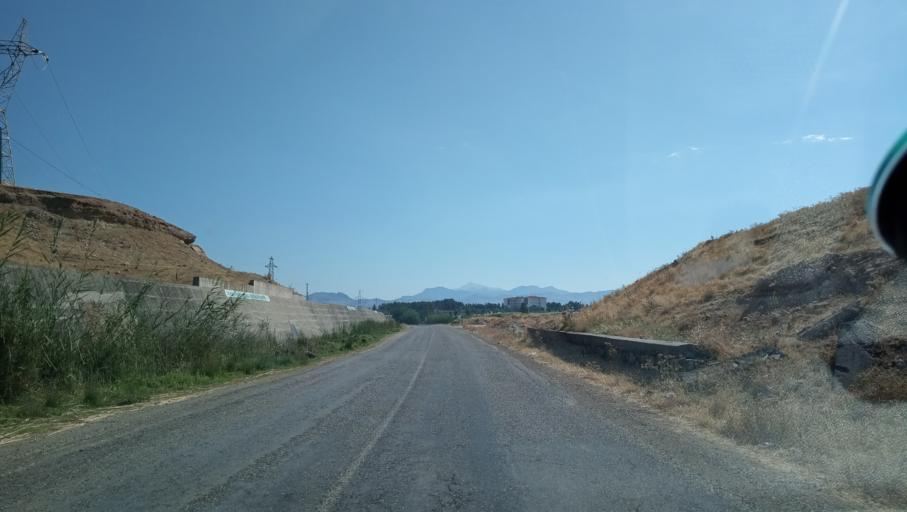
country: TR
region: Diyarbakir
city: Malabadi
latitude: 38.1333
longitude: 41.1872
